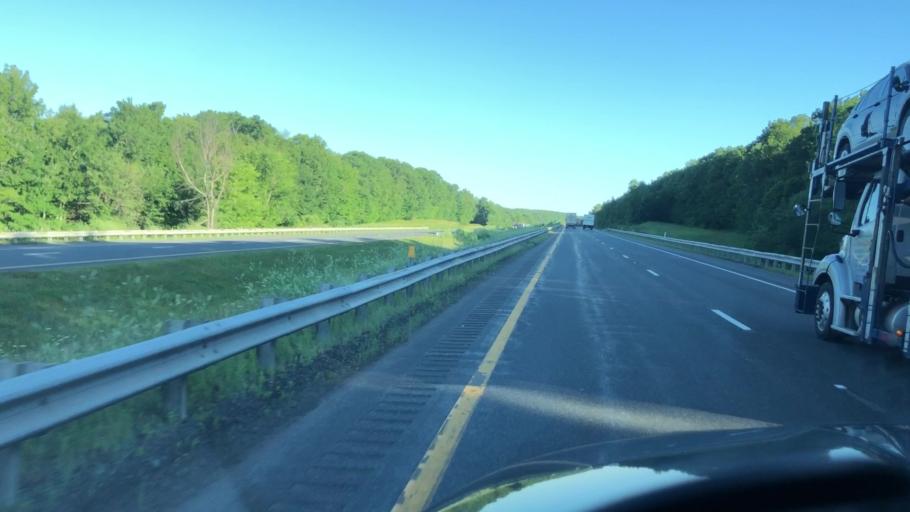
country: US
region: Massachusetts
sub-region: Berkshire County
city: Otis
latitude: 42.2028
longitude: -72.9434
